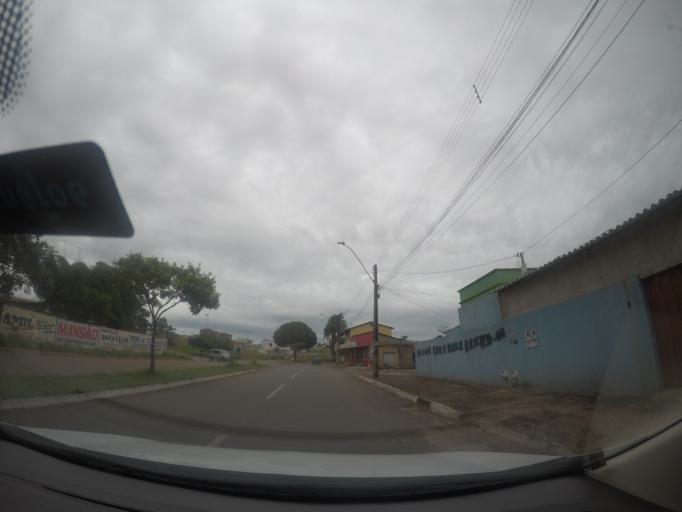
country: BR
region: Goias
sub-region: Goiania
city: Goiania
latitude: -16.6176
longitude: -49.3036
